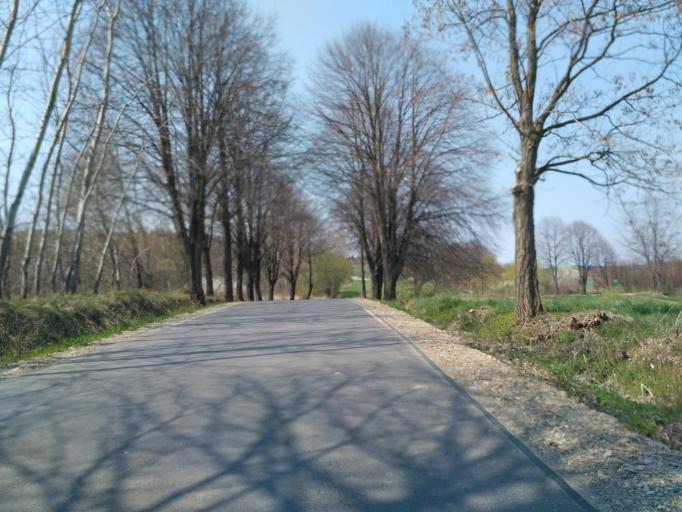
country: PL
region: Subcarpathian Voivodeship
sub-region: Powiat krosnienski
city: Chorkowka
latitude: 49.6398
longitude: 21.6834
